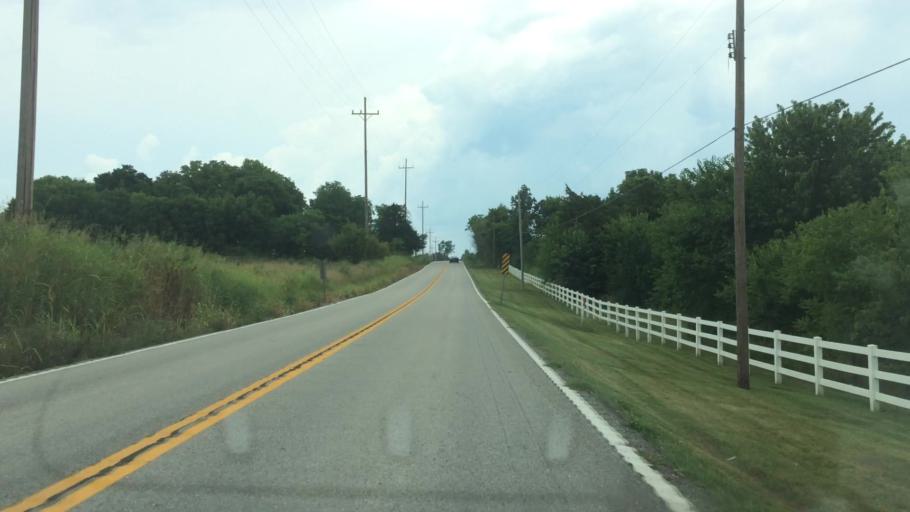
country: US
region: Missouri
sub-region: Greene County
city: Strafford
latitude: 37.2572
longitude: -93.1352
